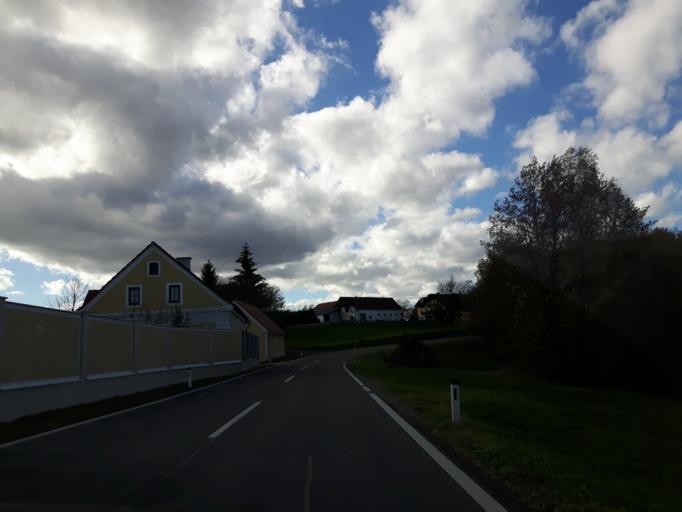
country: AT
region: Styria
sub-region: Politischer Bezirk Suedoststeiermark
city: Baumgarten bei Gnas
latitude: 46.9294
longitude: 15.7460
